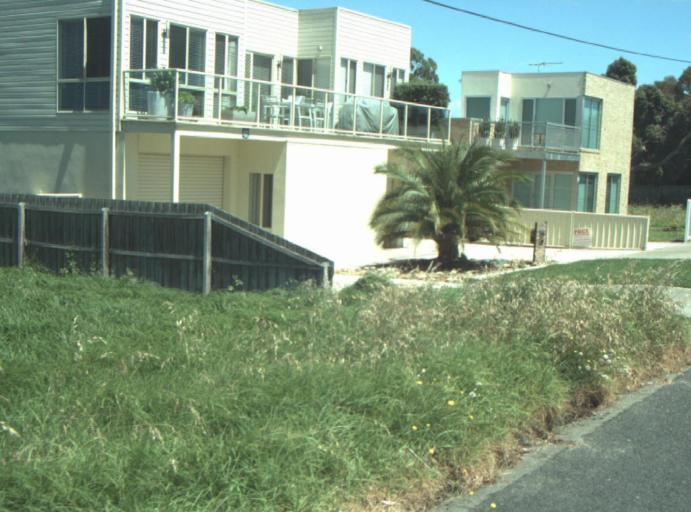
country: AU
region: Victoria
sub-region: Queenscliffe
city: Queenscliff
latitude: -38.1697
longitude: 144.7175
